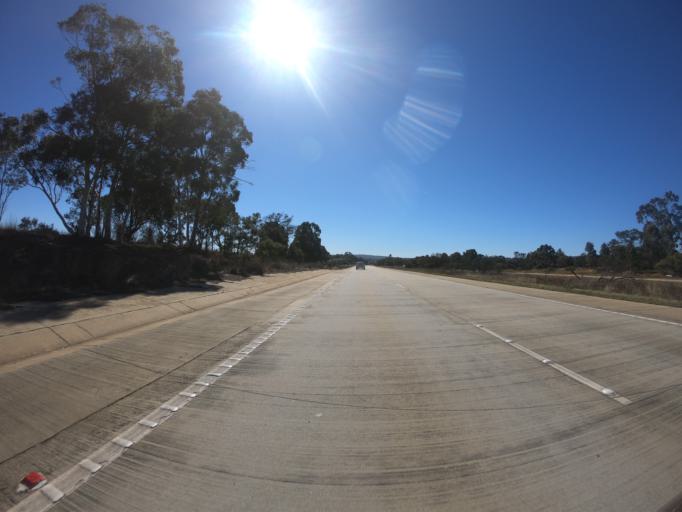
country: AU
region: New South Wales
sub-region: Yass Valley
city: Gundaroo
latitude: -35.1310
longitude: 149.3410
